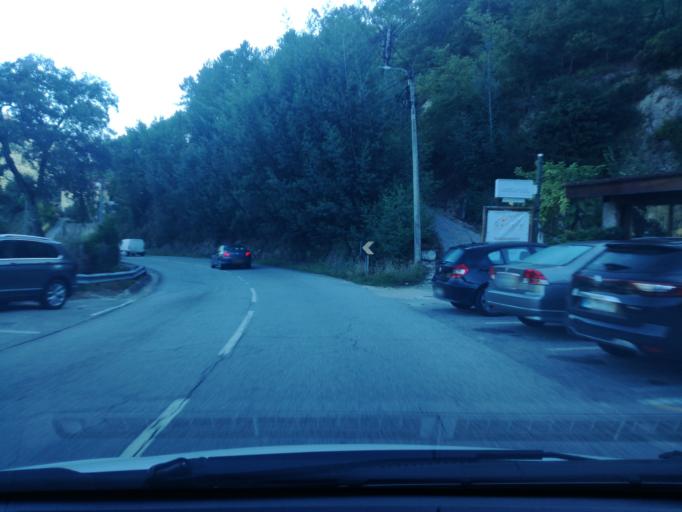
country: PT
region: Braga
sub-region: Vieira do Minho
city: Real
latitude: 41.6890
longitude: -8.1721
